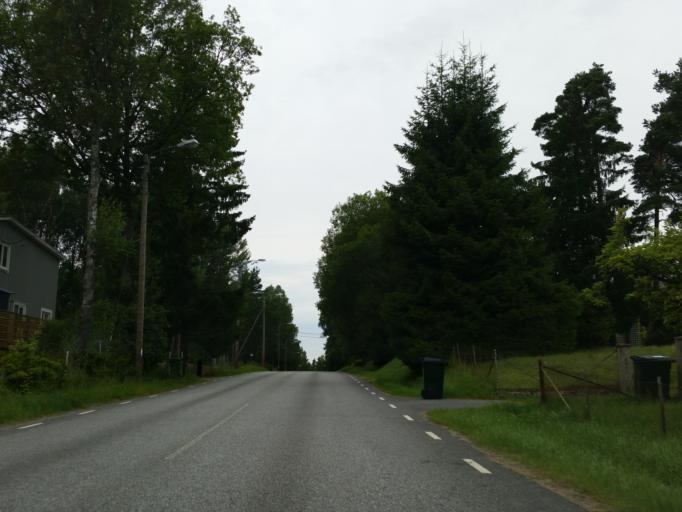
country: SE
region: Stockholm
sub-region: Sodertalje Kommun
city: Soedertaelje
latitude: 59.1990
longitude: 17.5784
